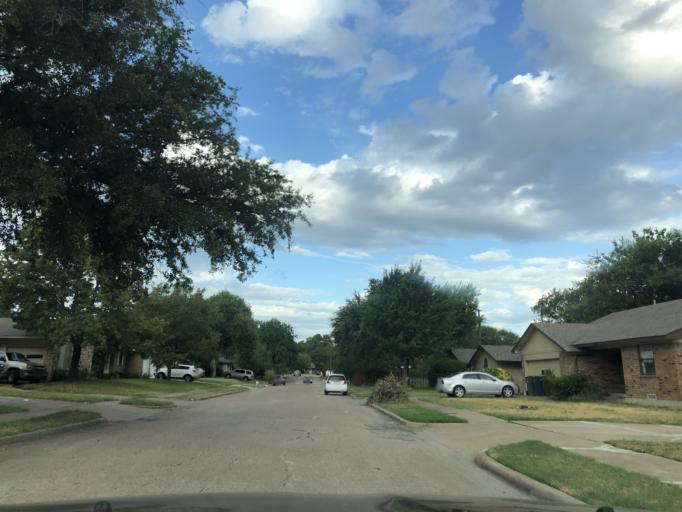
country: US
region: Texas
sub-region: Dallas County
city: Garland
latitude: 32.8720
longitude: -96.6508
